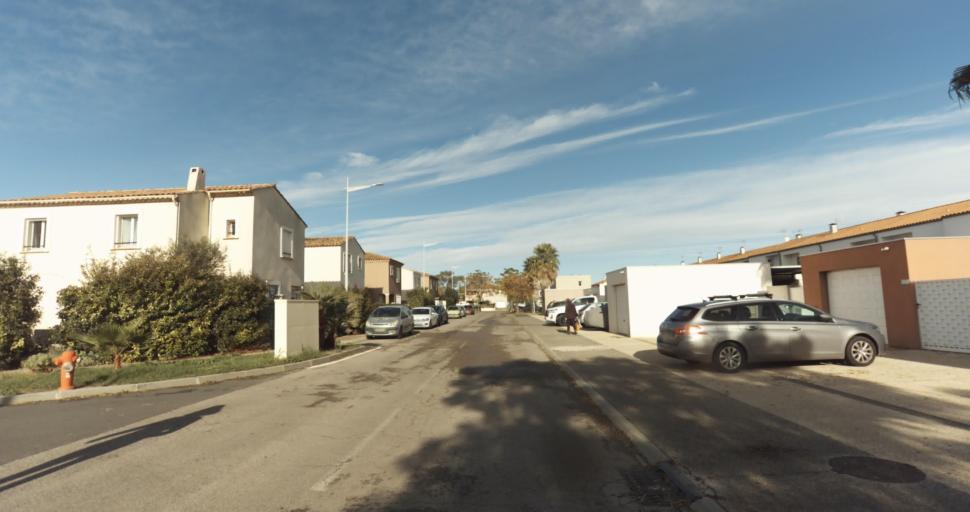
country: FR
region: Languedoc-Roussillon
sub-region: Departement du Gard
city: Aigues-Mortes
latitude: 43.5752
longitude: 4.1833
